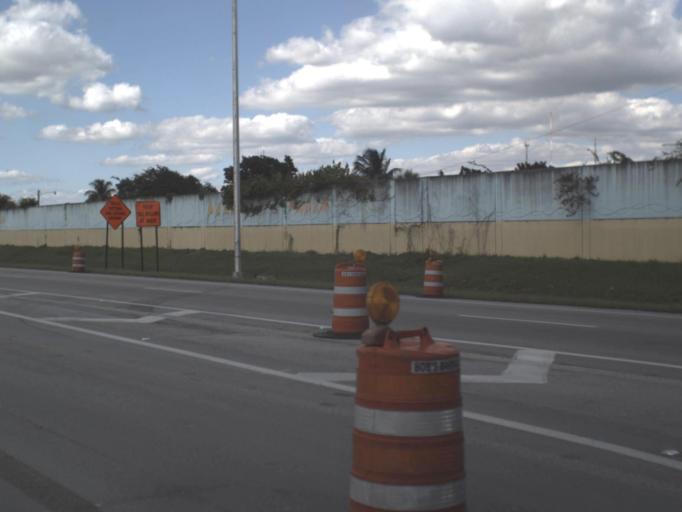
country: US
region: Florida
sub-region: Miami-Dade County
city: Norland
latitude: 25.9343
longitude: -80.2151
